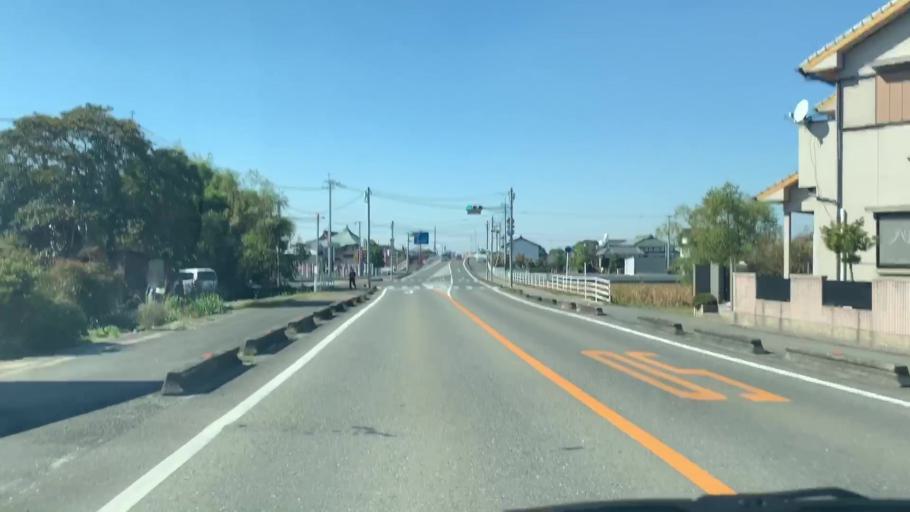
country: JP
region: Saga Prefecture
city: Kanzakimachi-kanzaki
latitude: 33.2625
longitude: 130.3979
